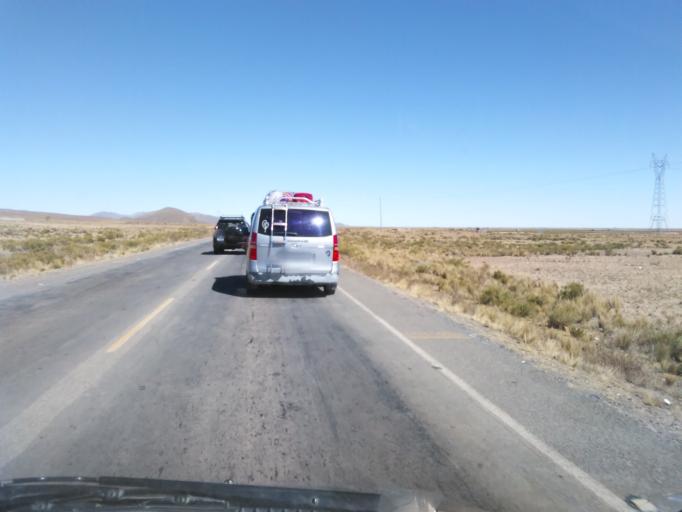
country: BO
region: Oruro
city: Machacamarca
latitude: -18.0716
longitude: -67.0057
